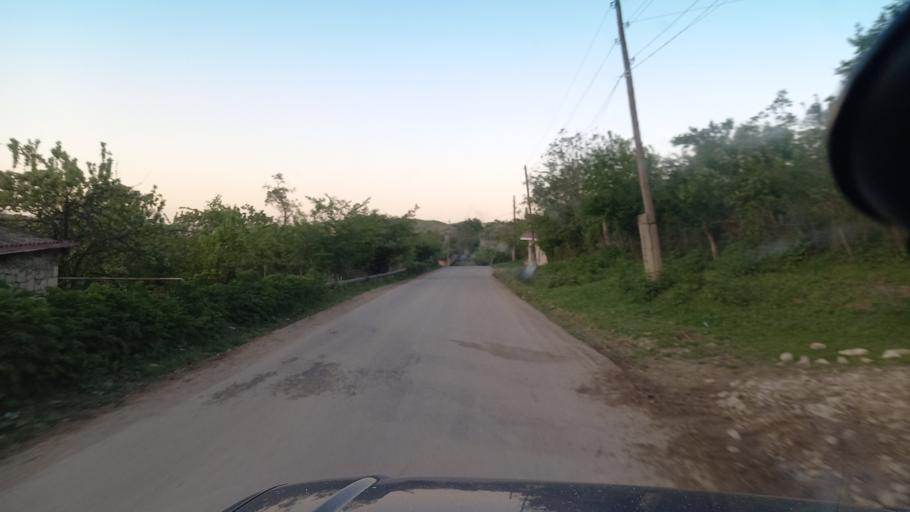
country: RU
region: Dagestan
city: Khuchni
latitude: 42.0280
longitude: 47.9676
